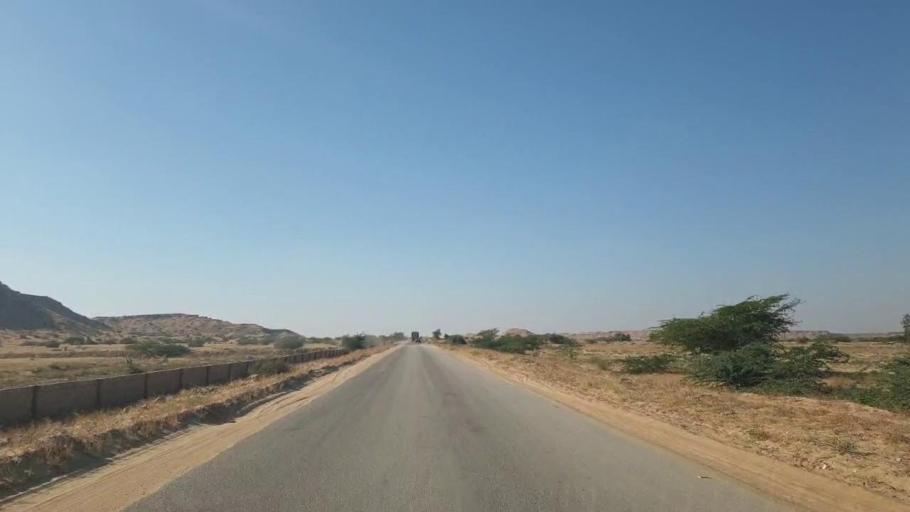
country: PK
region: Sindh
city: Gharo
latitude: 25.2171
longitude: 67.6265
